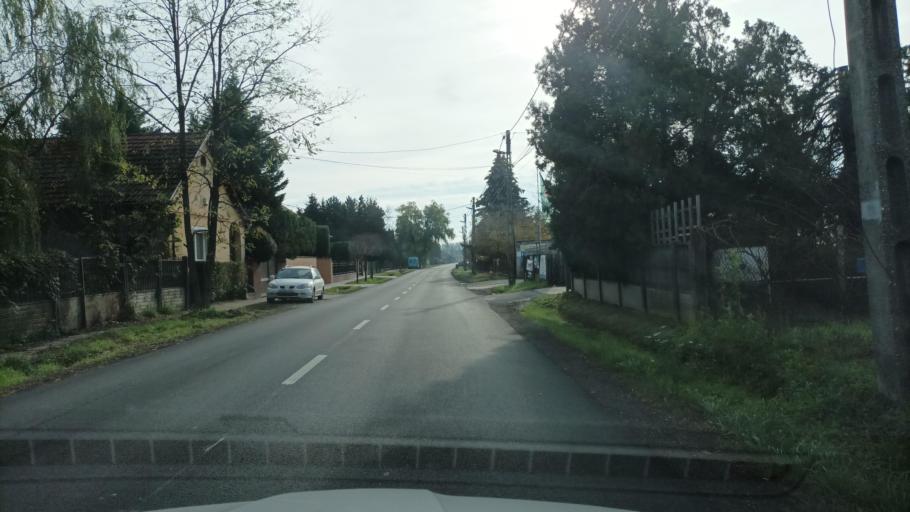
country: HU
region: Pest
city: Rackeve
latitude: 47.1472
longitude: 18.9463
